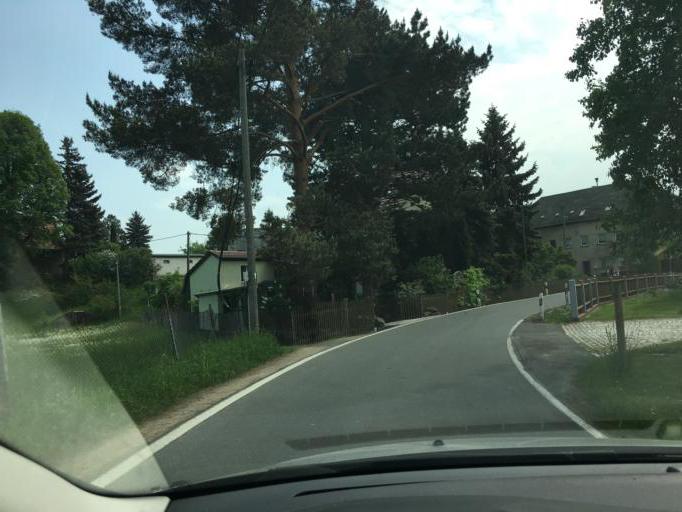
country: DE
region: Saxony
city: Rochlitz
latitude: 51.0693
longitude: 12.7923
